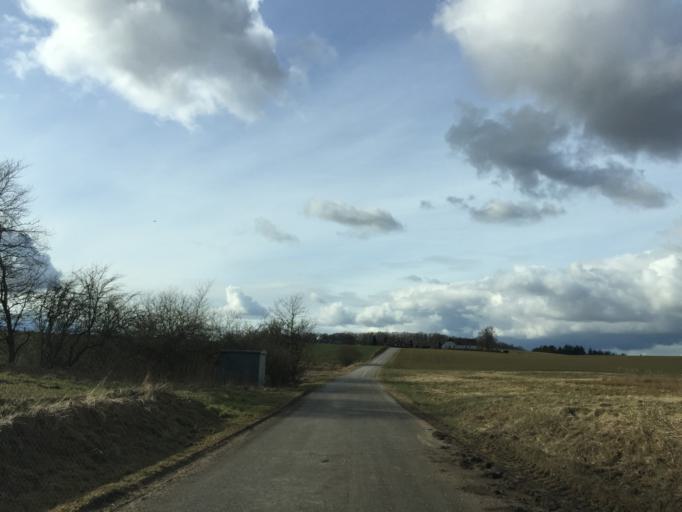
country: DK
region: Central Jutland
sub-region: Favrskov Kommune
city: Hammel
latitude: 56.1984
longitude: 9.7945
